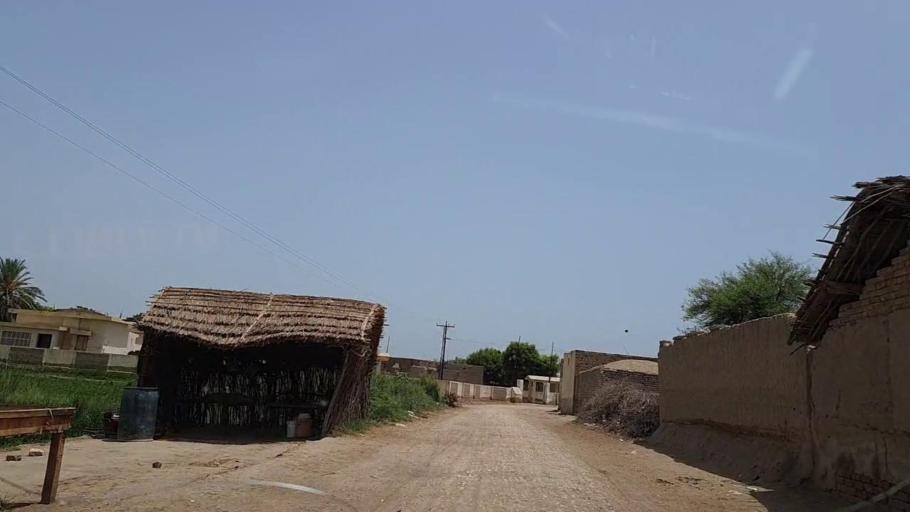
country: PK
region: Sindh
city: Tharu Shah
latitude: 26.9702
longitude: 68.0379
